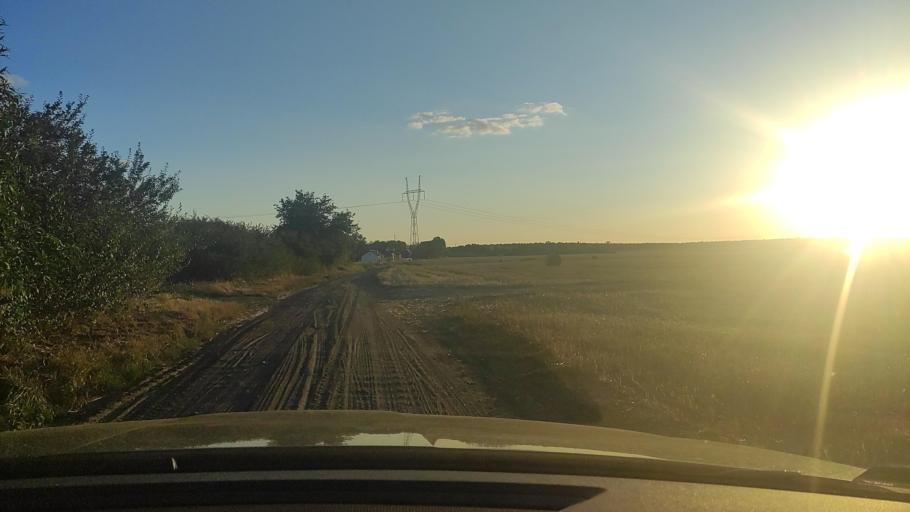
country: PL
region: Greater Poland Voivodeship
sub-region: Powiat poznanski
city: Kobylnica
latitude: 52.4547
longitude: 17.1389
